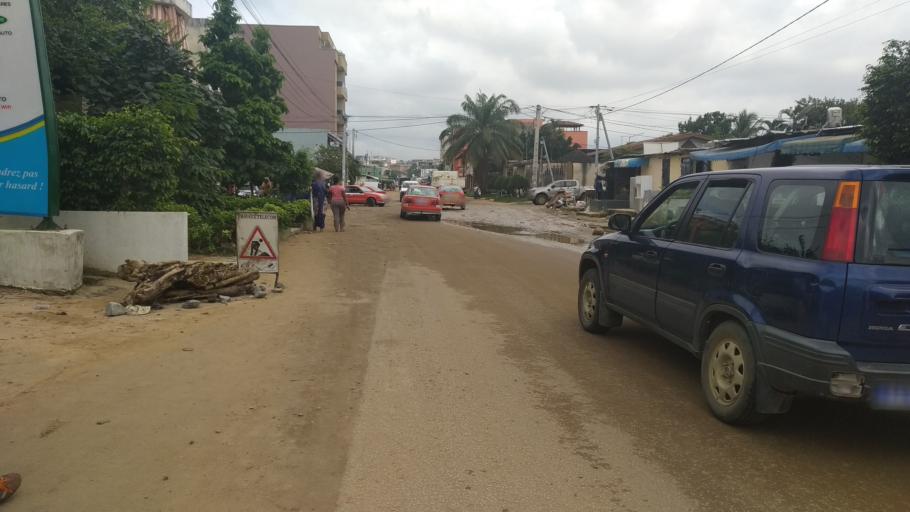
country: CI
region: Lagunes
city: Bingerville
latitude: 5.3680
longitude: -3.9575
